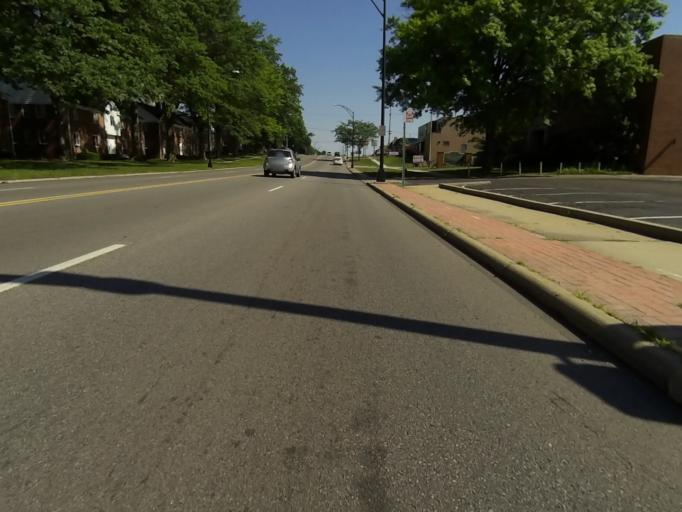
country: US
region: Ohio
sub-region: Summit County
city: Cuyahoga Falls
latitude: 41.1422
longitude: -81.5085
